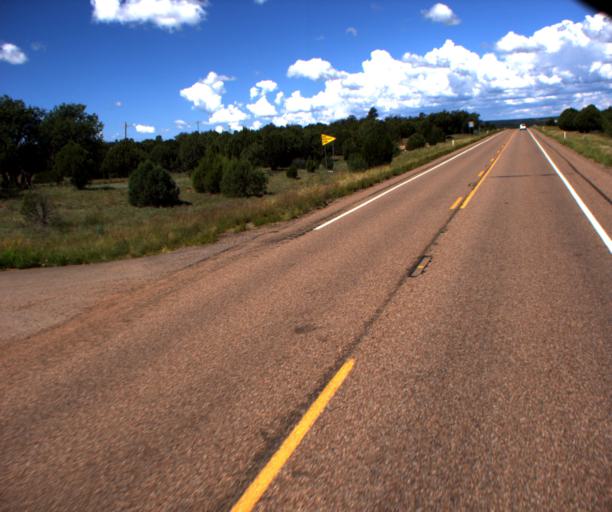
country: US
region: Arizona
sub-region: Navajo County
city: Linden
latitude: 34.3440
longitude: -110.2903
